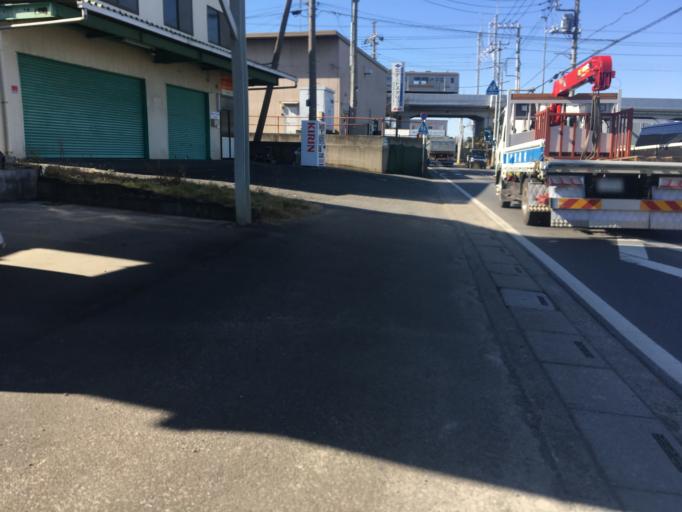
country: JP
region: Saitama
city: Asaka
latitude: 35.8264
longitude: 139.6098
